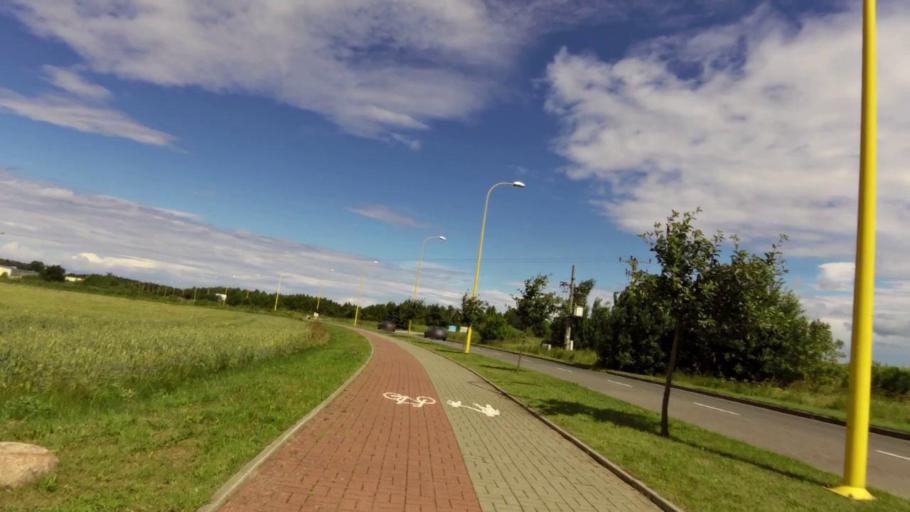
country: PL
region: West Pomeranian Voivodeship
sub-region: Powiat slawienski
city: Darlowo
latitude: 54.4420
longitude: 16.4060
